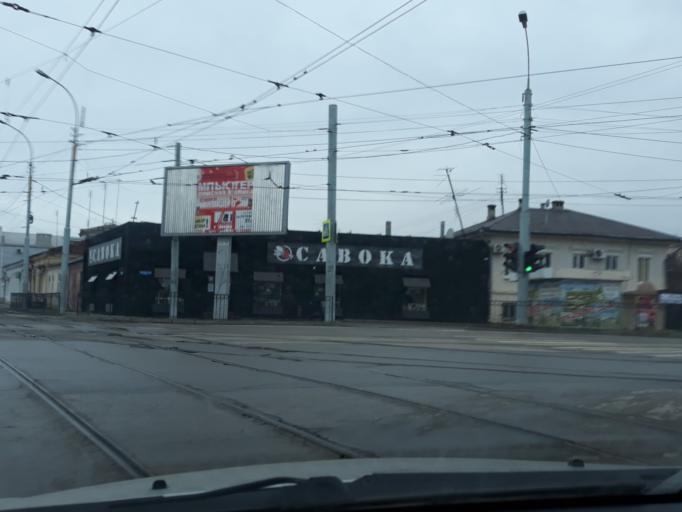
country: RU
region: Rostov
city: Taganrog
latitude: 47.2231
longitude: 38.9174
